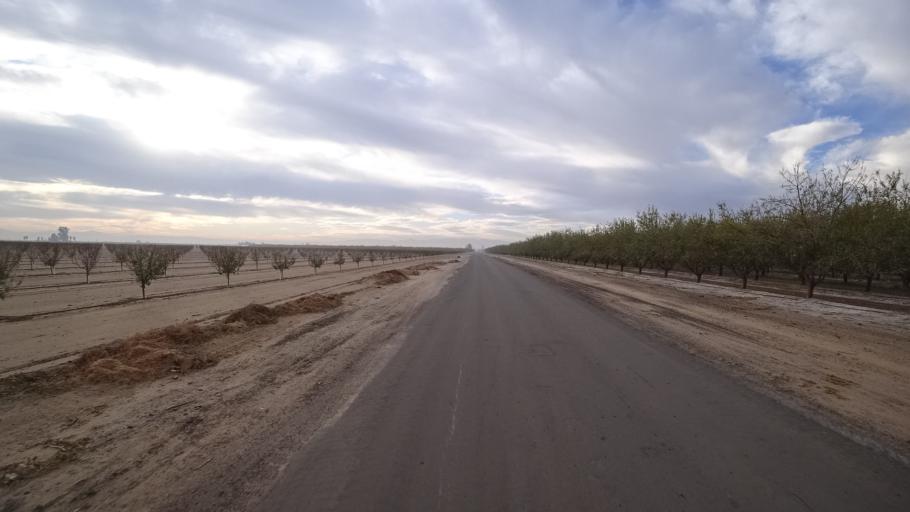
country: US
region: California
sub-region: Kern County
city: Rosedale
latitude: 35.4103
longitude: -119.1898
